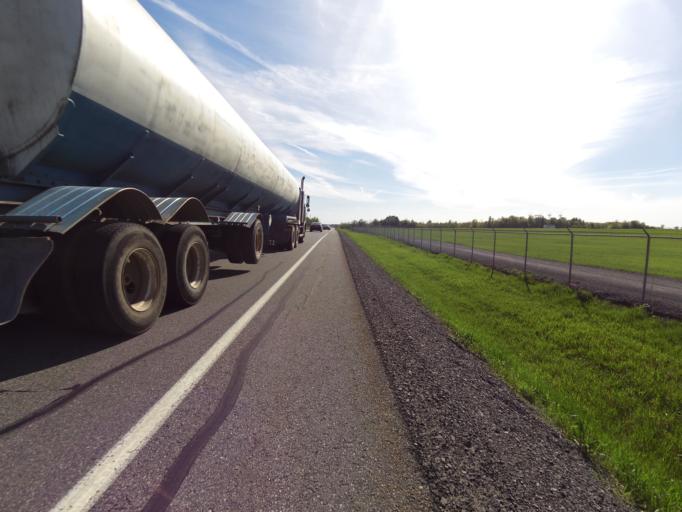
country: CA
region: Ontario
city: Ottawa
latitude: 45.3072
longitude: -75.6544
